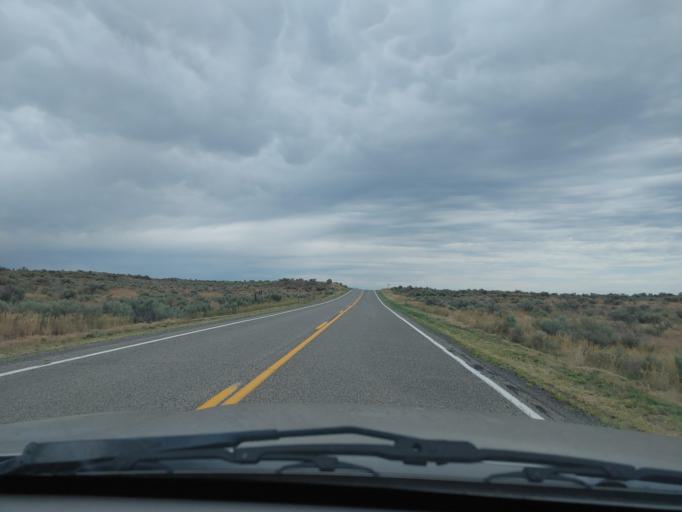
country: US
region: Idaho
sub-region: Lincoln County
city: Shoshone
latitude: 43.0898
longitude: -114.0922
